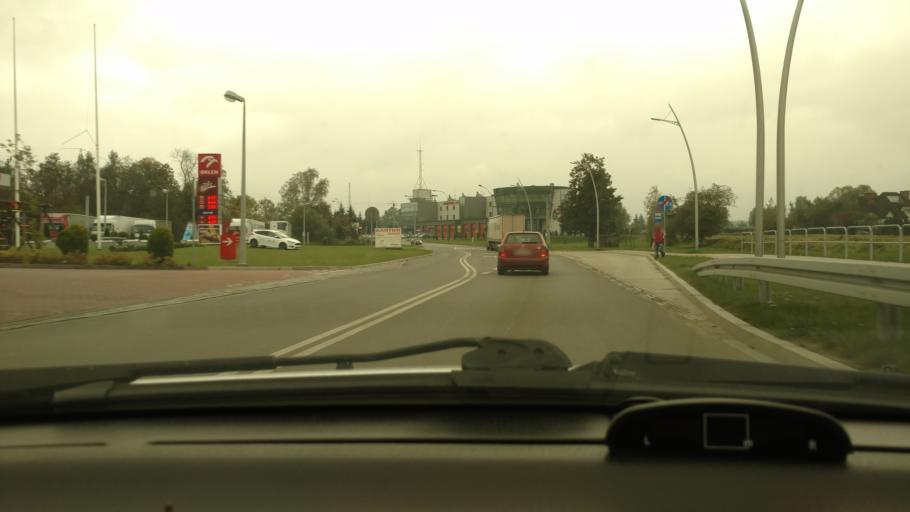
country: PL
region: Lesser Poland Voivodeship
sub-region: Powiat nowosadecki
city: Nowy Sacz
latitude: 49.6396
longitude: 20.6947
